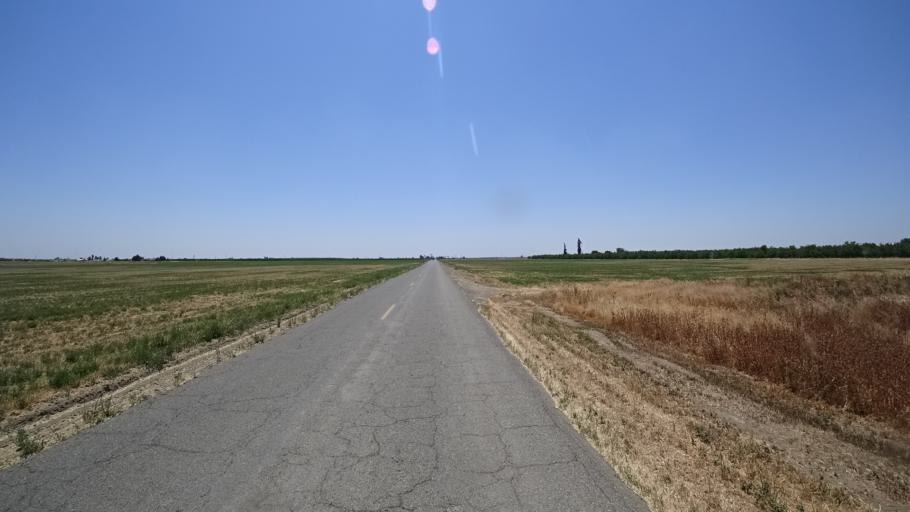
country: US
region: California
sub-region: Kings County
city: Lucerne
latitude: 36.3777
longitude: -119.7270
